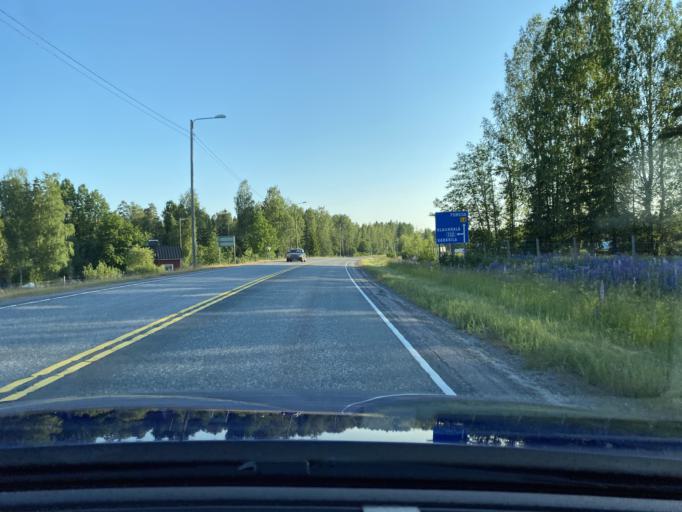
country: FI
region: Haeme
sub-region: Riihimaeki
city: Loppi
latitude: 60.7158
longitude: 24.4870
